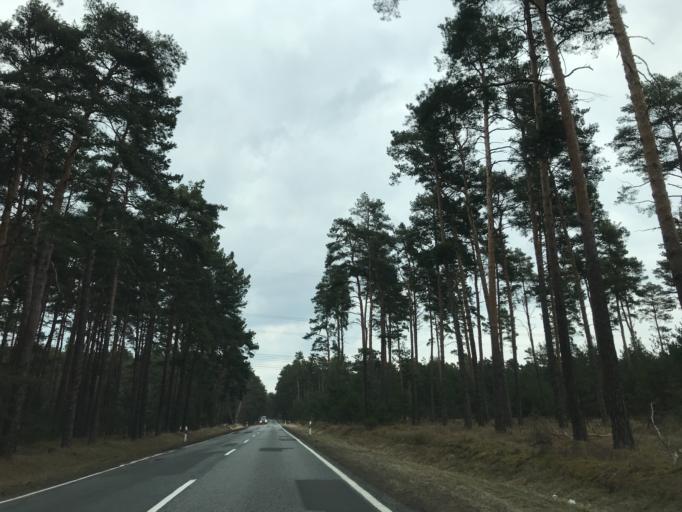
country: DE
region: Brandenburg
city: Fichtenwalde
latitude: 52.3034
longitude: 12.8685
